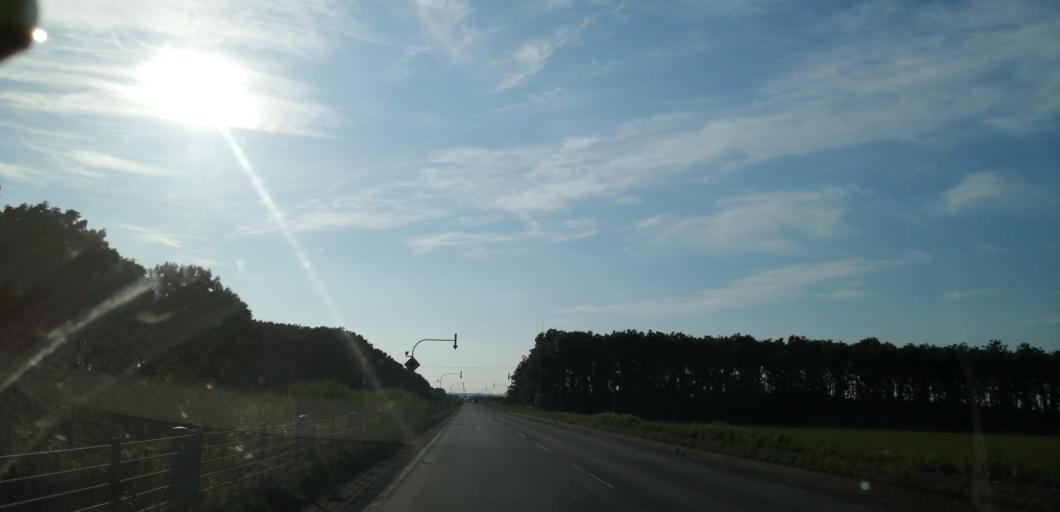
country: JP
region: Hokkaido
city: Kitahiroshima
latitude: 42.9777
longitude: 141.6419
